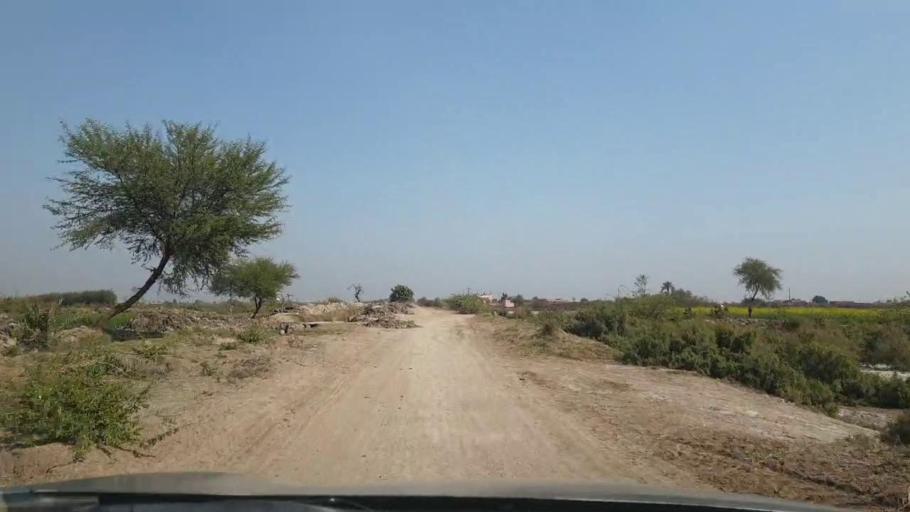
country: PK
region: Sindh
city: Berani
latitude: 25.6599
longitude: 68.8844
